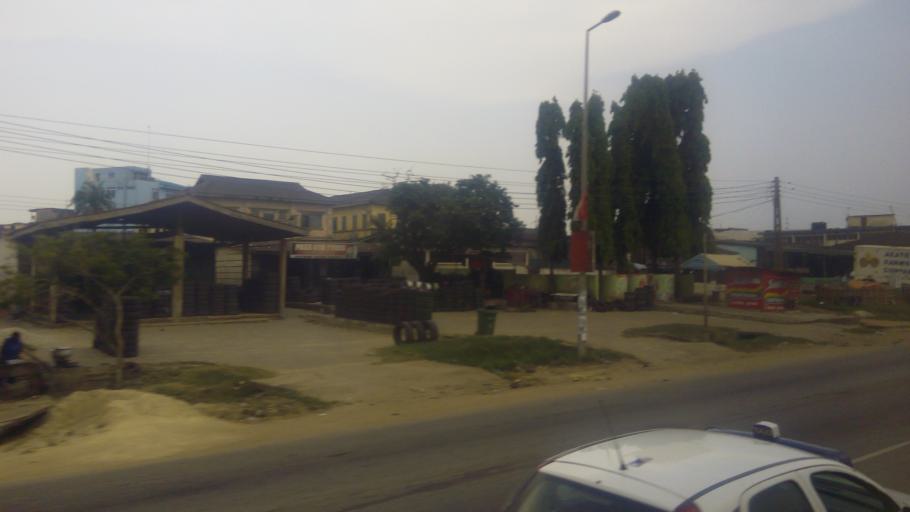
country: GH
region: Western
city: Takoradi
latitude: 4.9003
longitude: -1.7670
